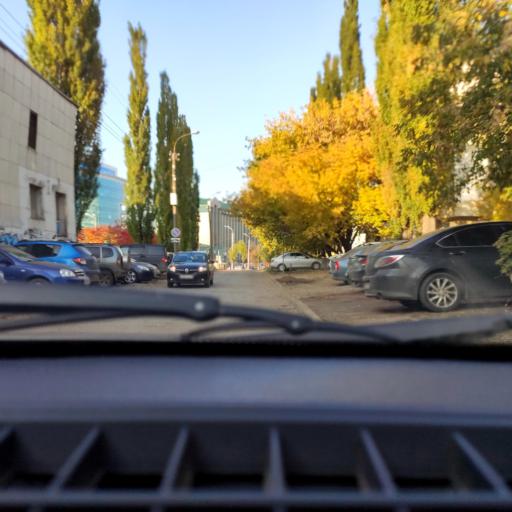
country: RU
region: Bashkortostan
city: Ufa
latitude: 54.7458
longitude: 55.9820
